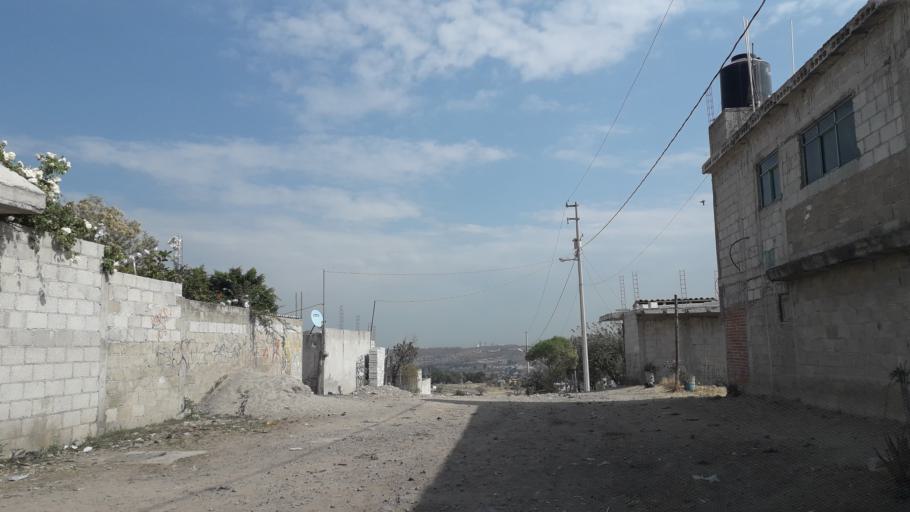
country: MX
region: Puebla
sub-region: Puebla
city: San Andres Azumiatla
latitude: 18.9074
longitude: -98.2486
